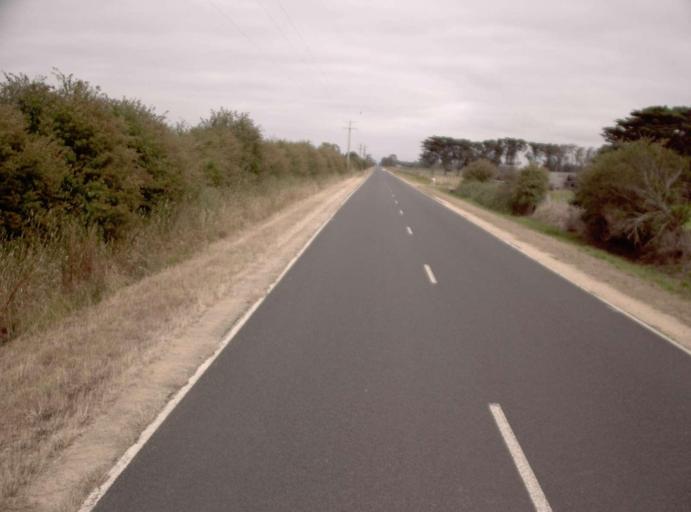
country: AU
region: Victoria
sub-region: Wellington
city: Sale
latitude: -38.0528
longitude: 146.9584
